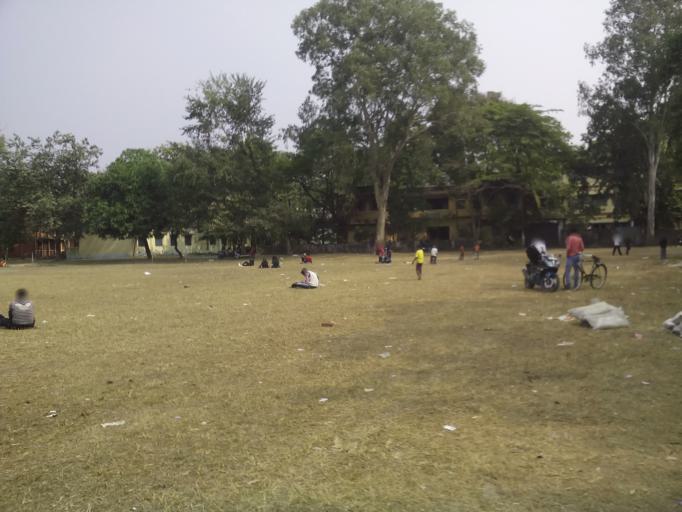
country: IN
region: West Bengal
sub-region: Darjiling
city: Shiliguri
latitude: 26.7081
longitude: 88.4326
